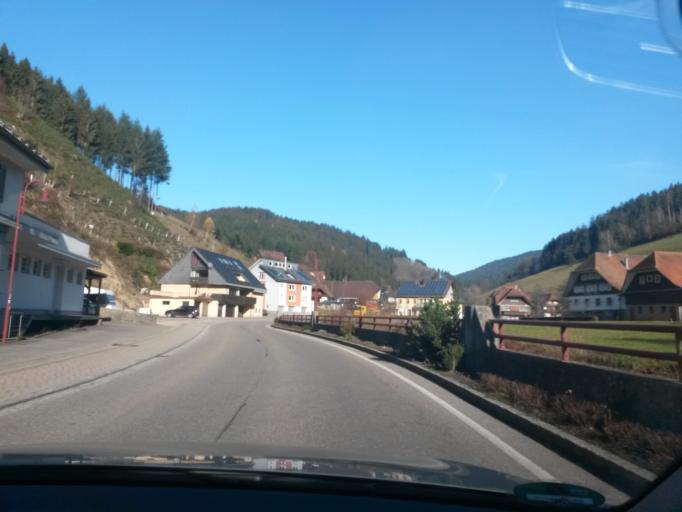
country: DE
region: Baden-Wuerttemberg
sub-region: Karlsruhe Region
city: Bad Rippoldsau-Schapbach
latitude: 48.3790
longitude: 8.2956
